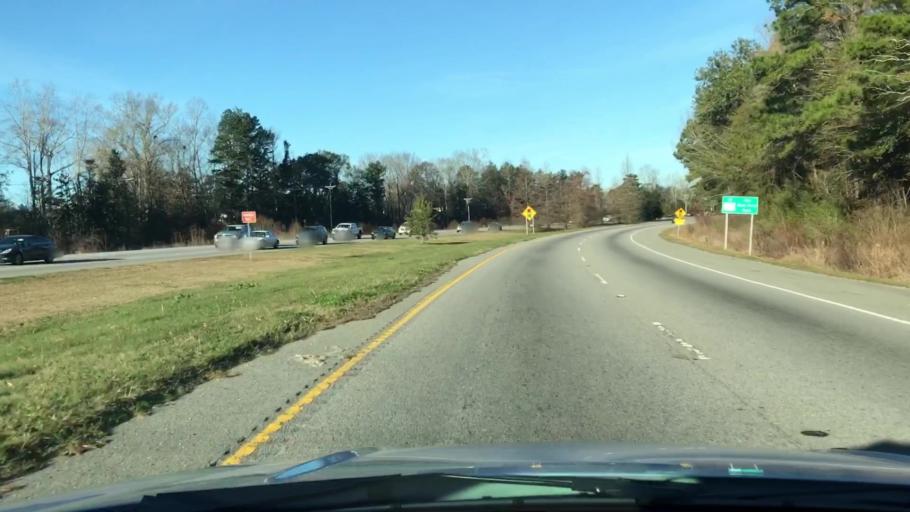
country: US
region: South Carolina
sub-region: Charleston County
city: Shell Point
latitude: 32.8114
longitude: -80.0557
